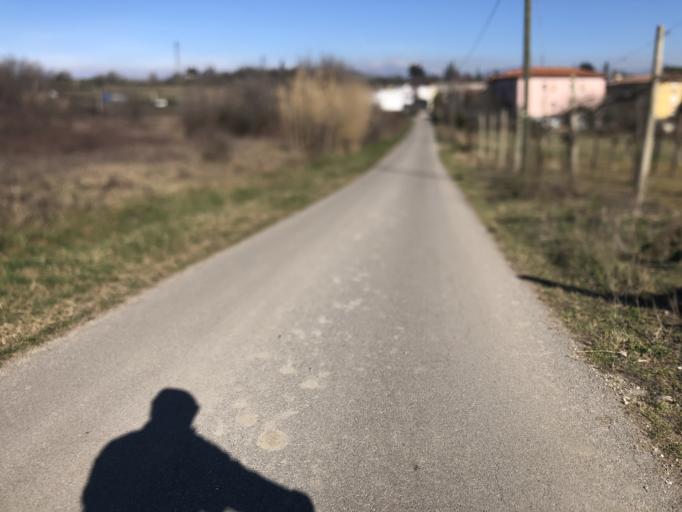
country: IT
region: Veneto
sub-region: Provincia di Verona
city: Sona
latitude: 45.4403
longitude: 10.8160
